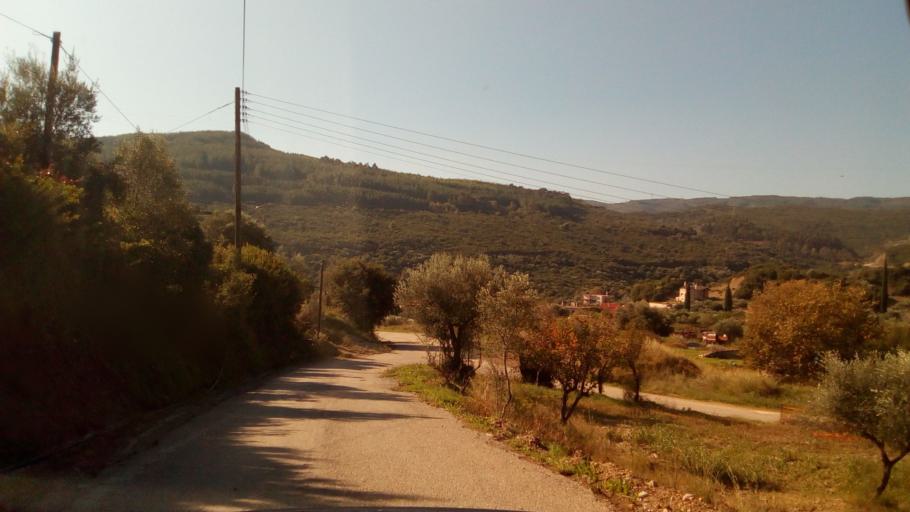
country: GR
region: West Greece
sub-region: Nomos Aitolias kai Akarnanias
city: Nafpaktos
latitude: 38.4083
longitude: 21.7820
